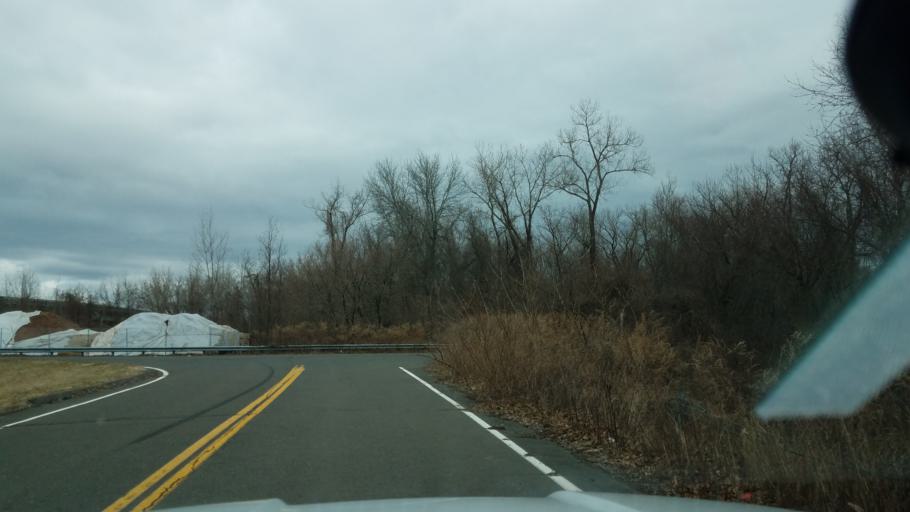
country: US
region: Connecticut
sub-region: Hartford County
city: Wethersfield
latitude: 41.7109
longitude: -72.6419
